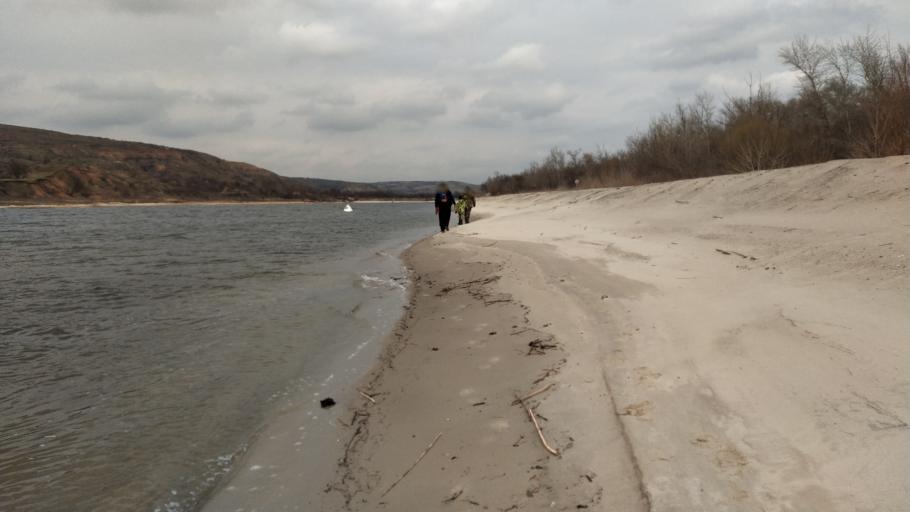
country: RU
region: Rostov
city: Semikarakorsk
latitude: 47.5553
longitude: 40.6725
